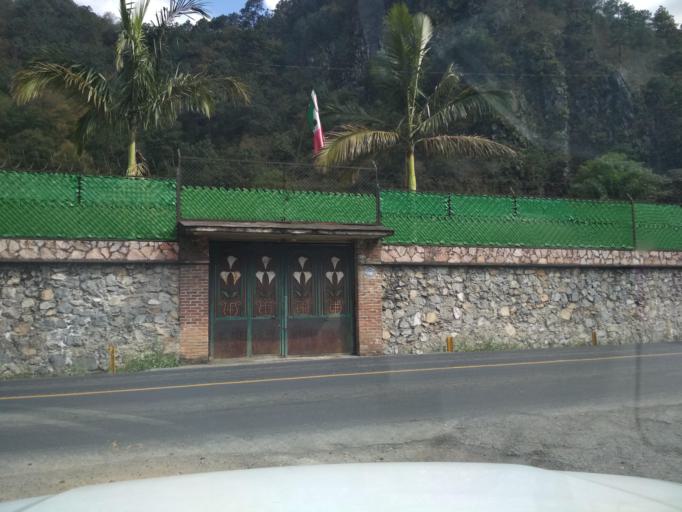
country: MX
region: Veracruz
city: Jalapilla
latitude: 18.7975
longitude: -97.1015
